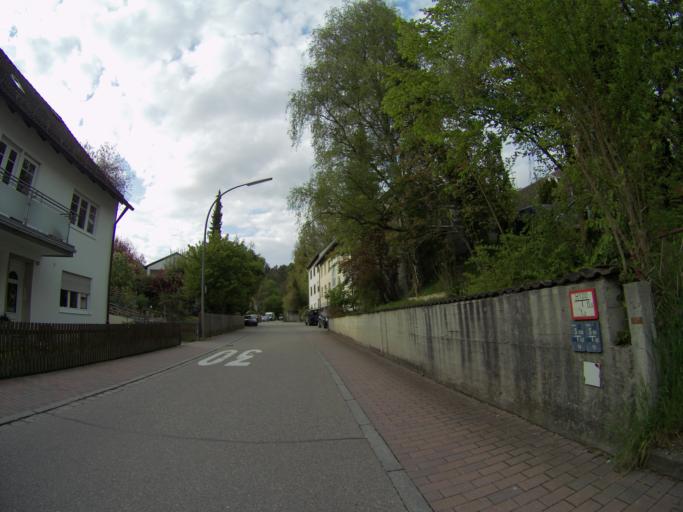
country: DE
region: Bavaria
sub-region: Upper Bavaria
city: Freising
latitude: 48.4105
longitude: 11.7599
